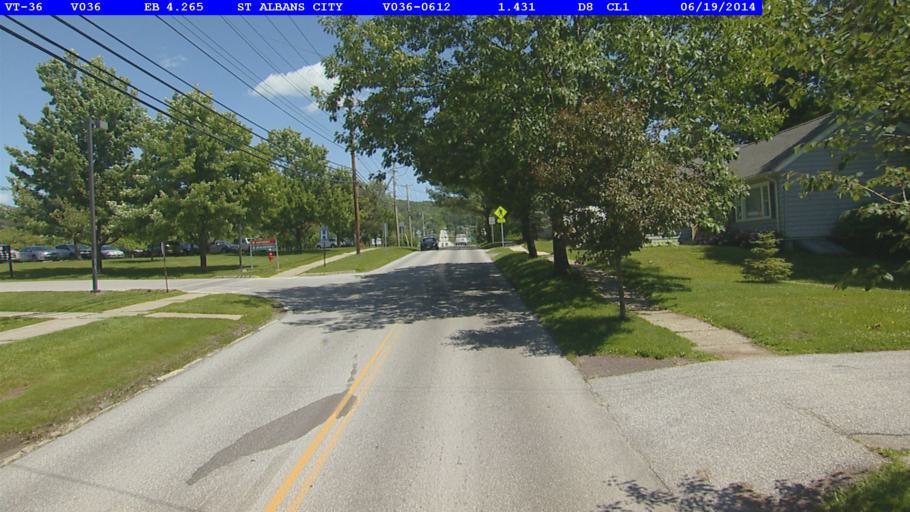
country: US
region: Vermont
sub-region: Franklin County
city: Saint Albans
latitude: 44.8066
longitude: -73.0731
